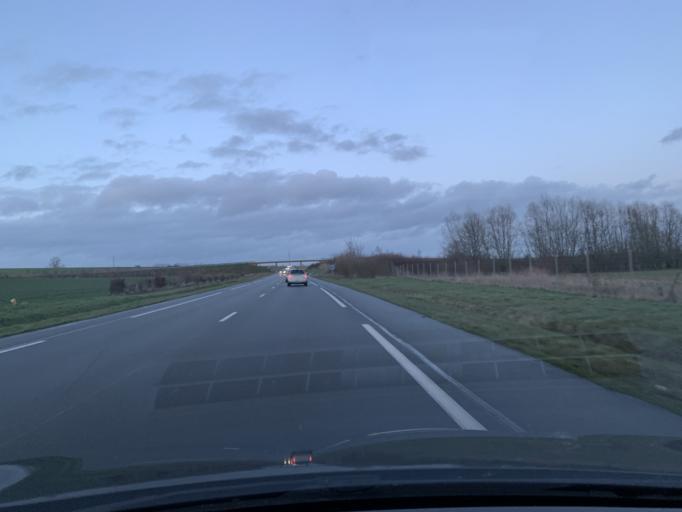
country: FR
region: Nord-Pas-de-Calais
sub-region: Departement du Nord
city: Escaudoeuvres
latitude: 50.1535
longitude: 3.2926
